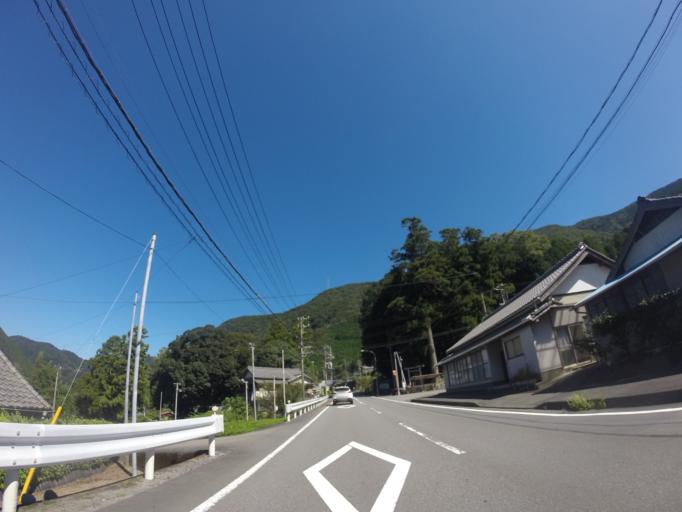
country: JP
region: Shizuoka
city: Kanaya
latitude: 34.8885
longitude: 138.1191
